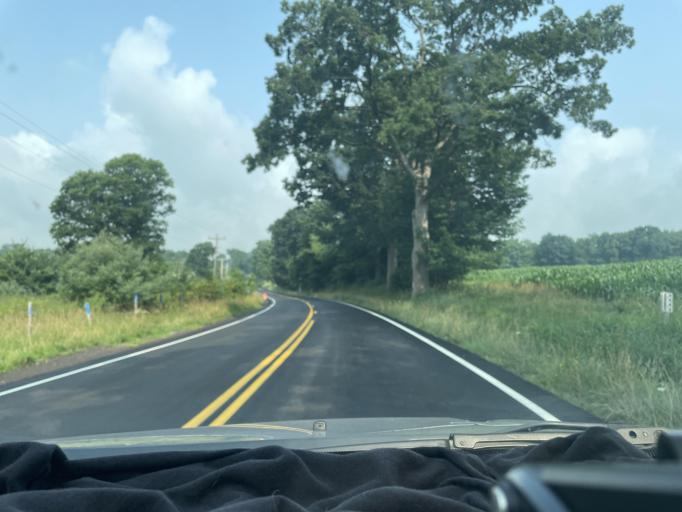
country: US
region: Maryland
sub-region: Garrett County
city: Mountain Lake Park
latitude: 39.2978
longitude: -79.3777
